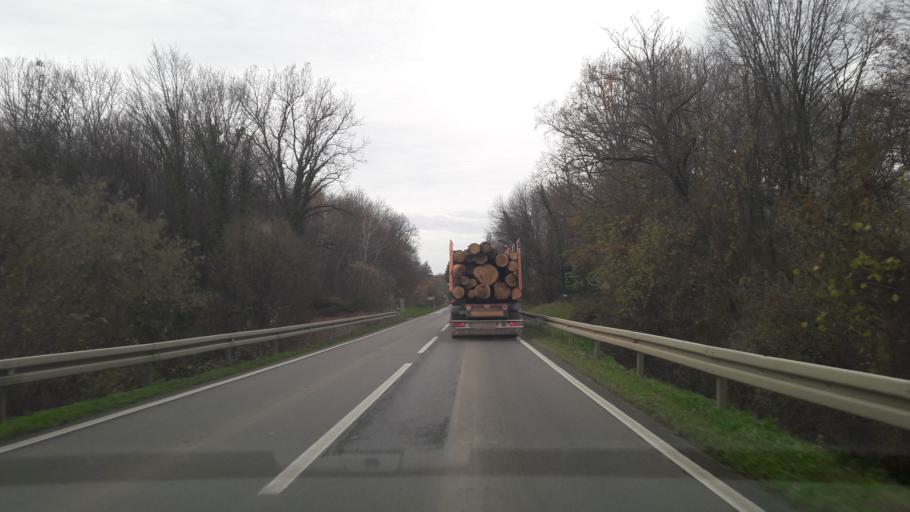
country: HR
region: Virovitick-Podravska
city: Orahovica
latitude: 45.5446
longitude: 17.9125
